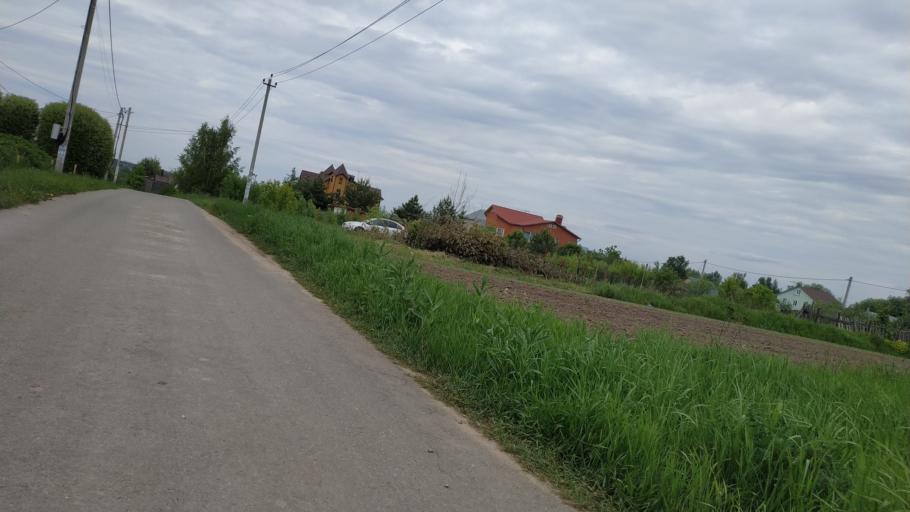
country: RU
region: Moskovskaya
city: Ostrovtsy
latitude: 55.5241
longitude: 37.9958
